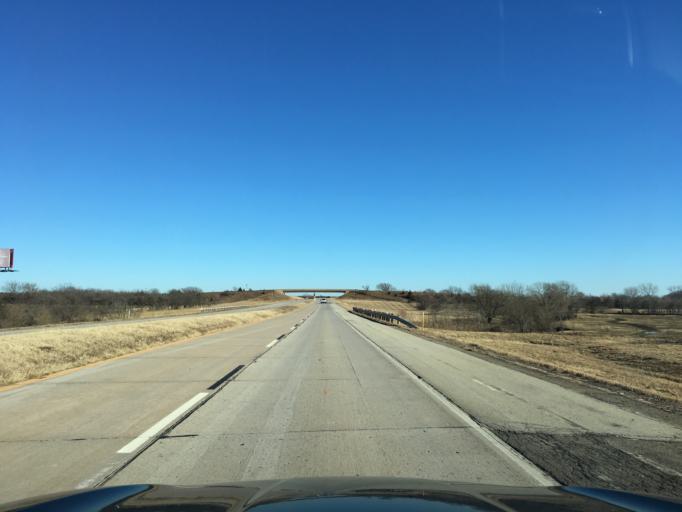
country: US
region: Oklahoma
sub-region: Payne County
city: Yale
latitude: 36.2245
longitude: -96.7179
